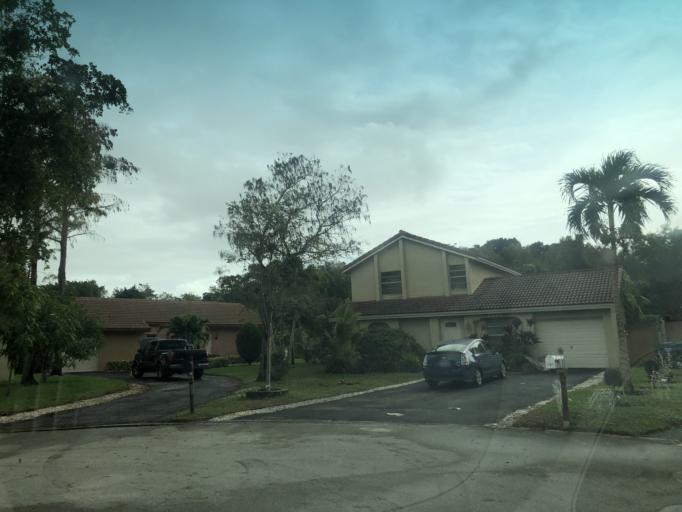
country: US
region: Florida
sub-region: Broward County
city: Tamarac
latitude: 26.2457
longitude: -80.2468
